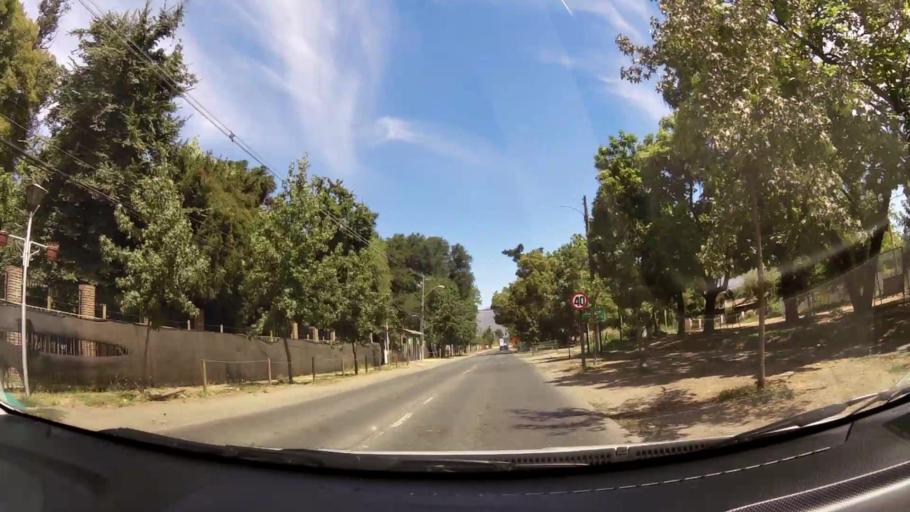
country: CL
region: O'Higgins
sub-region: Provincia de Cachapoal
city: Graneros
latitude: -34.0689
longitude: -70.7215
